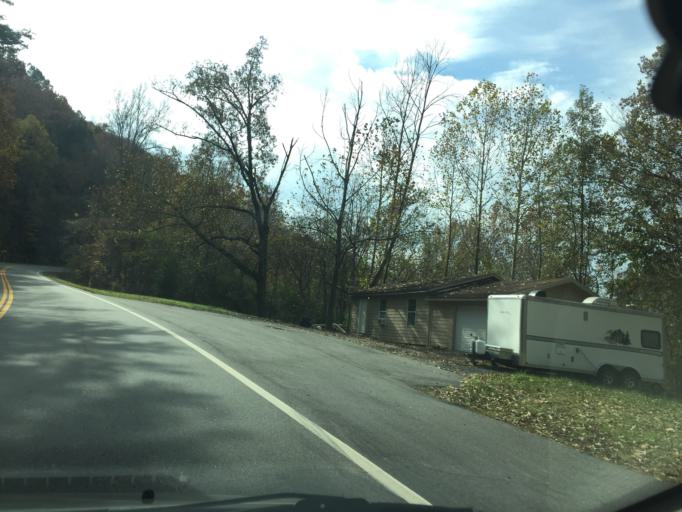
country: US
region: Georgia
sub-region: Dade County
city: Trenton
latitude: 34.8538
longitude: -85.4957
